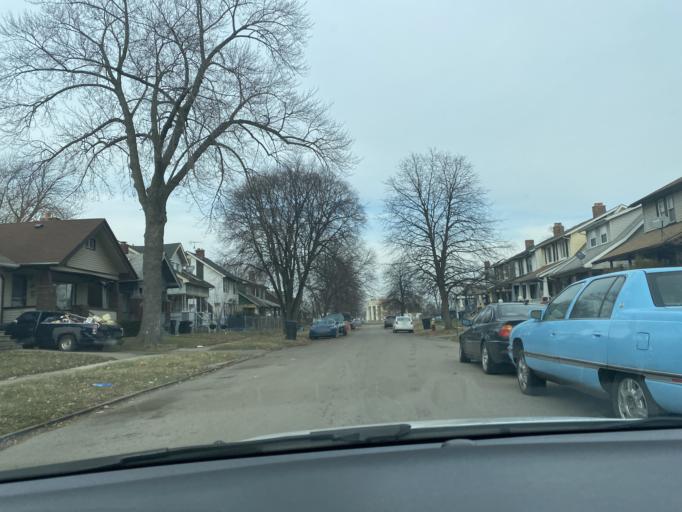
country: US
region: Michigan
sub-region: Wayne County
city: Dearborn
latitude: 42.3669
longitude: -83.1423
